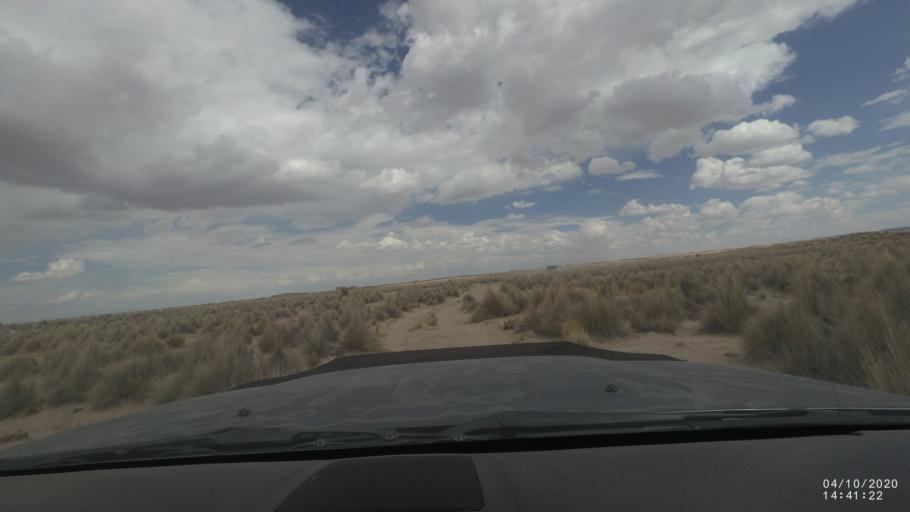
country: BO
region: Oruro
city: Poopo
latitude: -18.6823
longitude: -67.4908
